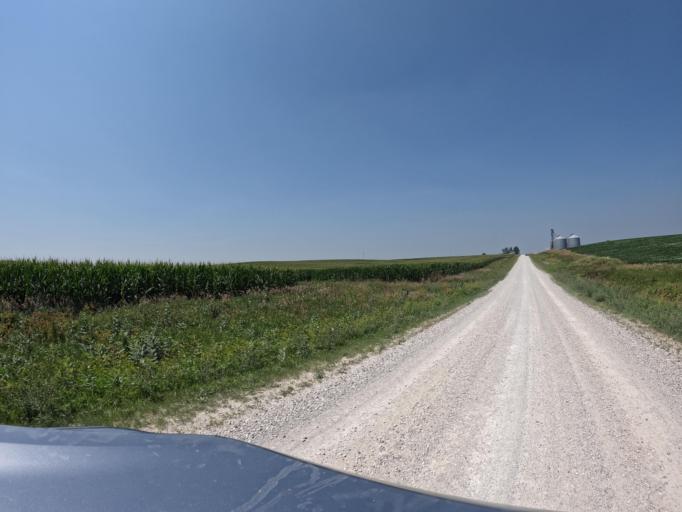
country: US
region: Iowa
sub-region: Keokuk County
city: Sigourney
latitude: 41.3309
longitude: -92.2384
